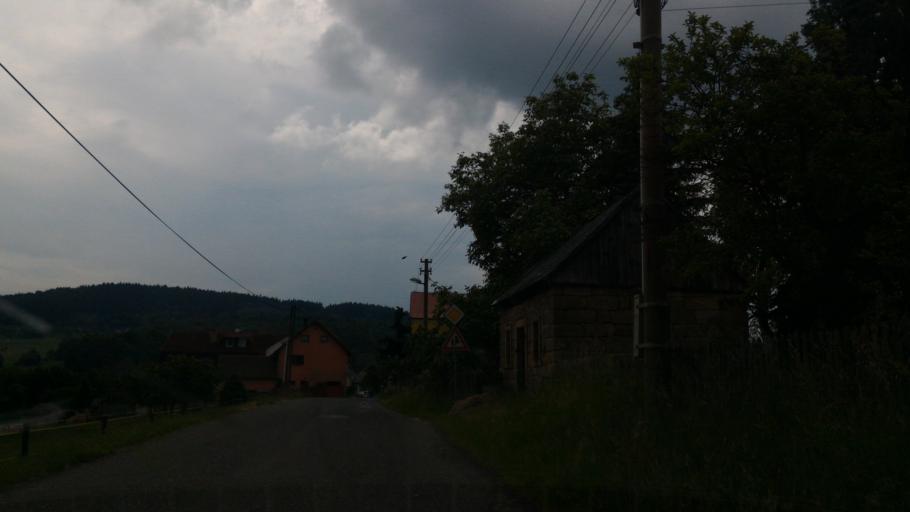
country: CZ
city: Hradek nad Nisou
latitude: 50.8309
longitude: 14.8345
